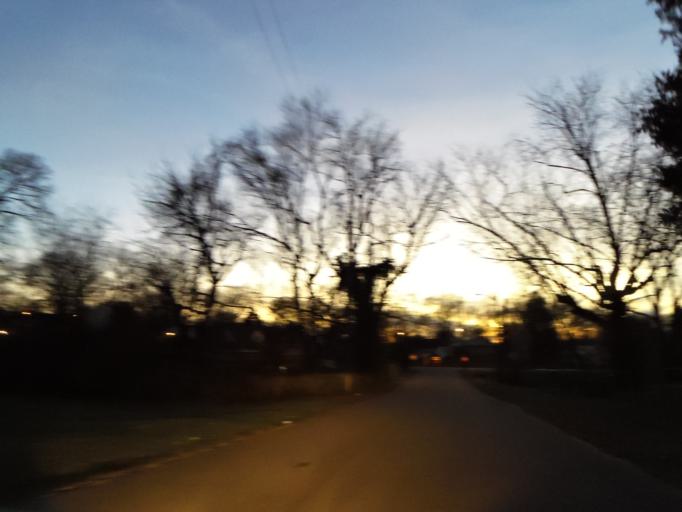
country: US
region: Tennessee
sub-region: Knox County
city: Knoxville
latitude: 35.9914
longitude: -83.8824
